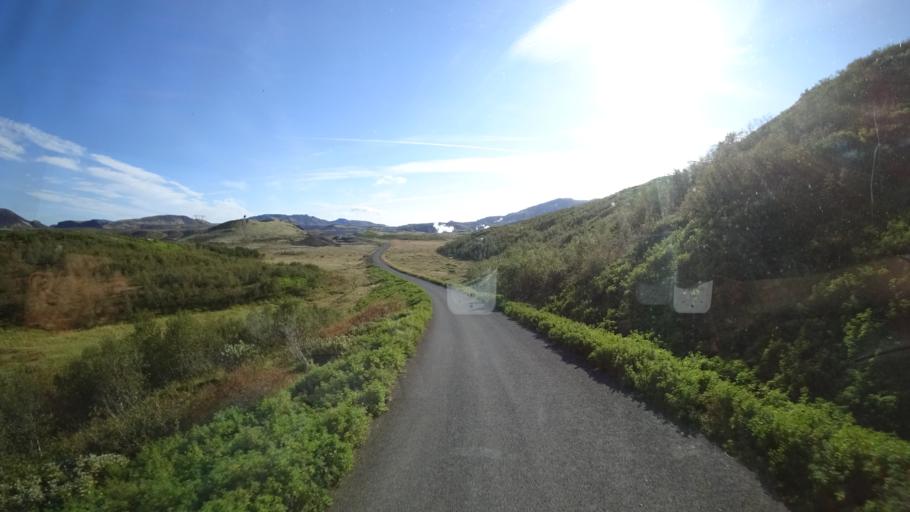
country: IS
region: South
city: Hveragerdi
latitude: 64.1308
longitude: -21.2511
